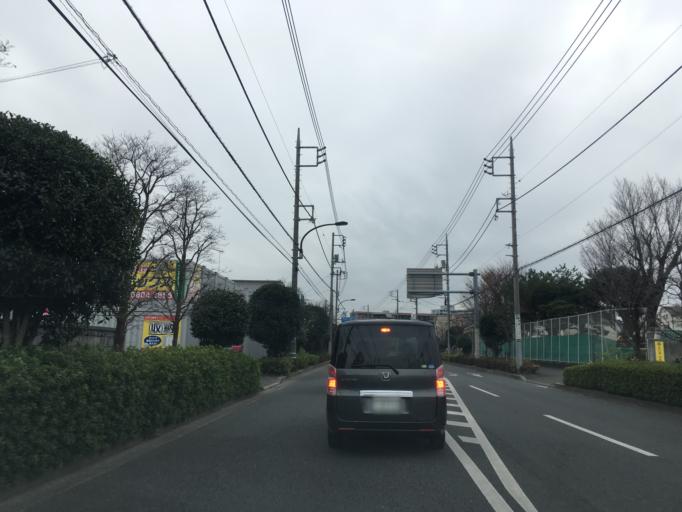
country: JP
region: Tokyo
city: Tanashicho
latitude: 35.7390
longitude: 139.5006
